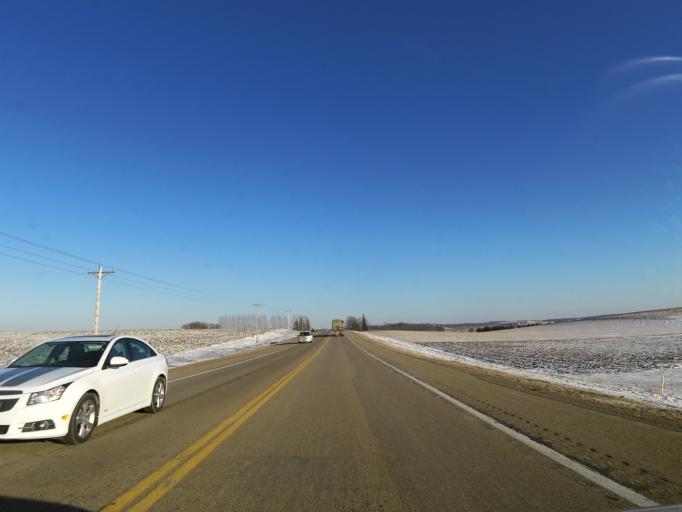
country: US
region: Minnesota
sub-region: Rice County
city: Lonsdale
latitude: 44.4860
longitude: -93.5008
